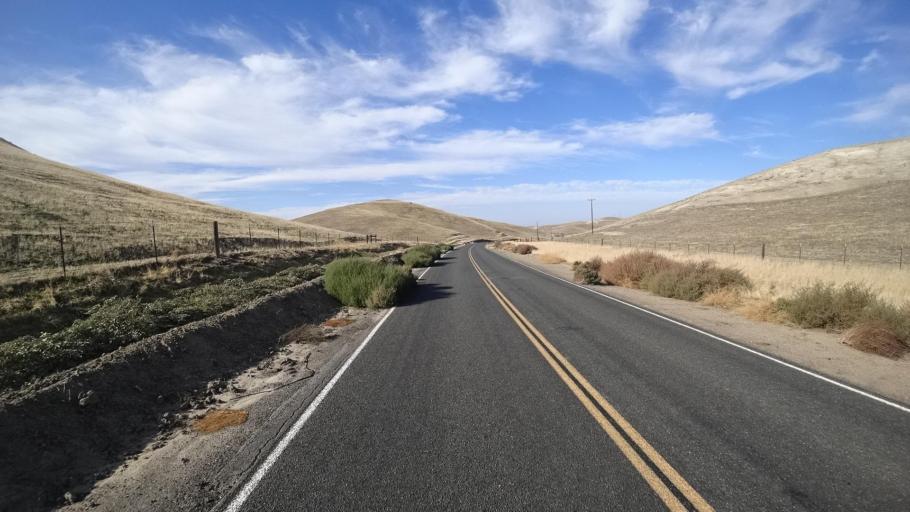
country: US
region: California
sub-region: Kern County
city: Oildale
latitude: 35.6092
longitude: -118.9042
